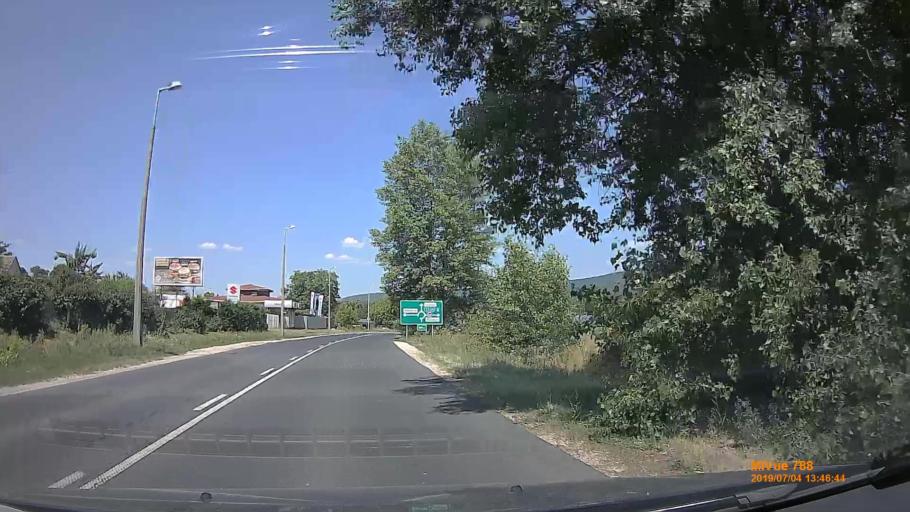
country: HU
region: Komarom-Esztergom
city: Tatabanya
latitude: 47.5899
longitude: 18.3792
